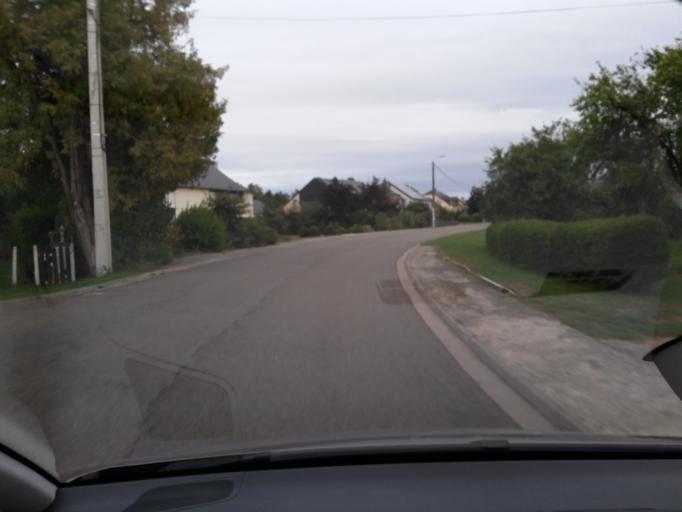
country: BE
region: Wallonia
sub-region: Province du Luxembourg
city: Etalle
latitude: 49.6600
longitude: 5.5768
